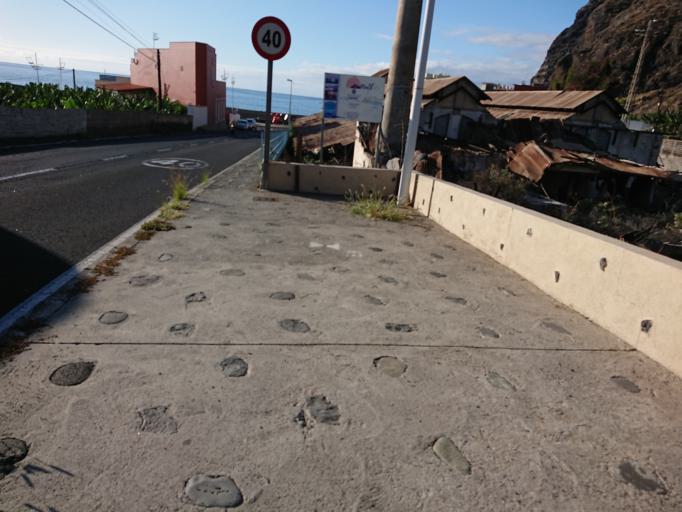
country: ES
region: Canary Islands
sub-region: Provincia de Santa Cruz de Tenerife
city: Tazacorte
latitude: 28.6475
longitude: -17.9428
